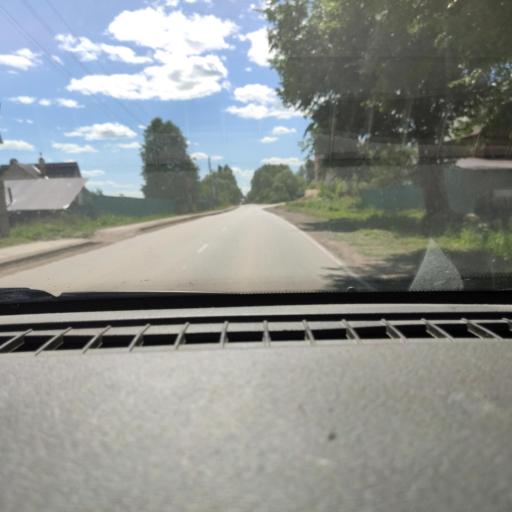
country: RU
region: Perm
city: Chaykovskaya
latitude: 58.1075
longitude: 55.5790
